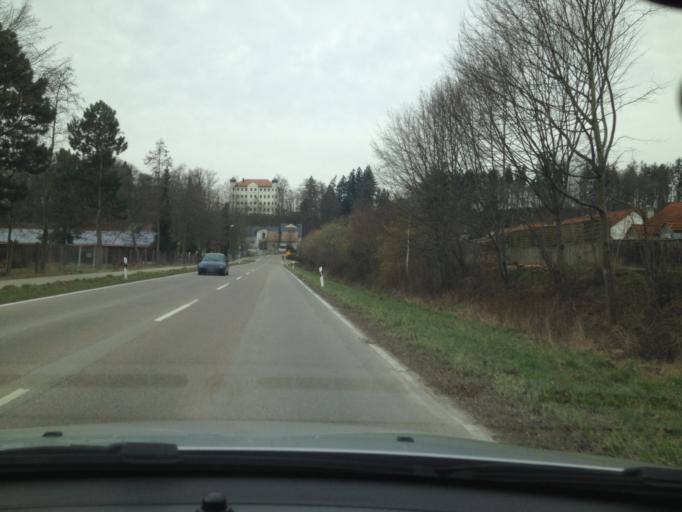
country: DE
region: Bavaria
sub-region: Swabia
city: Wehringen
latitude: 48.2707
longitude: 10.7931
